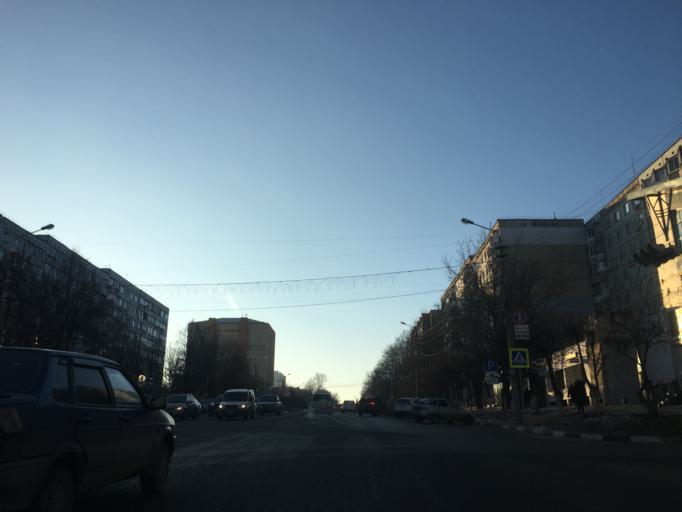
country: RU
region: Tula
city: Tula
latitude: 54.1943
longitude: 37.5909
